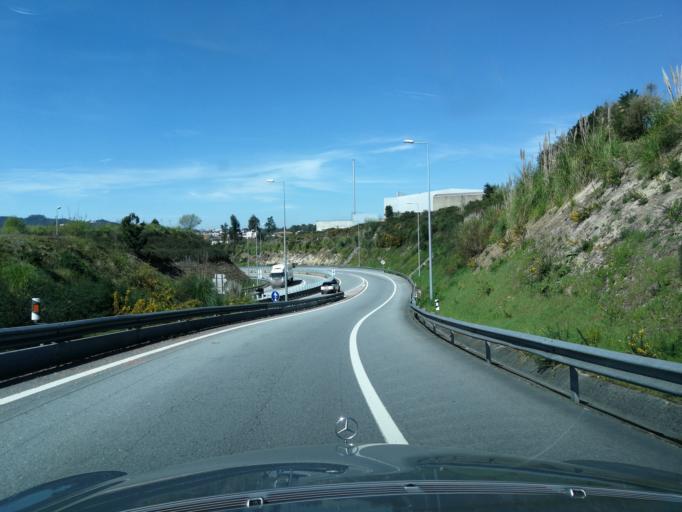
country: PT
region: Braga
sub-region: Vila Nova de Famalicao
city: Vila Nova de Famalicao
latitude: 41.3901
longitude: -8.5155
